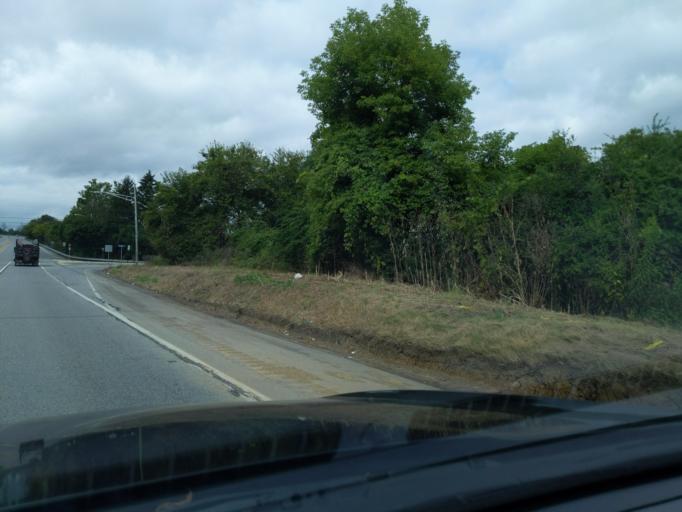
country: US
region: Pennsylvania
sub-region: Blair County
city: Hollidaysburg
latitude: 40.4203
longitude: -78.3922
